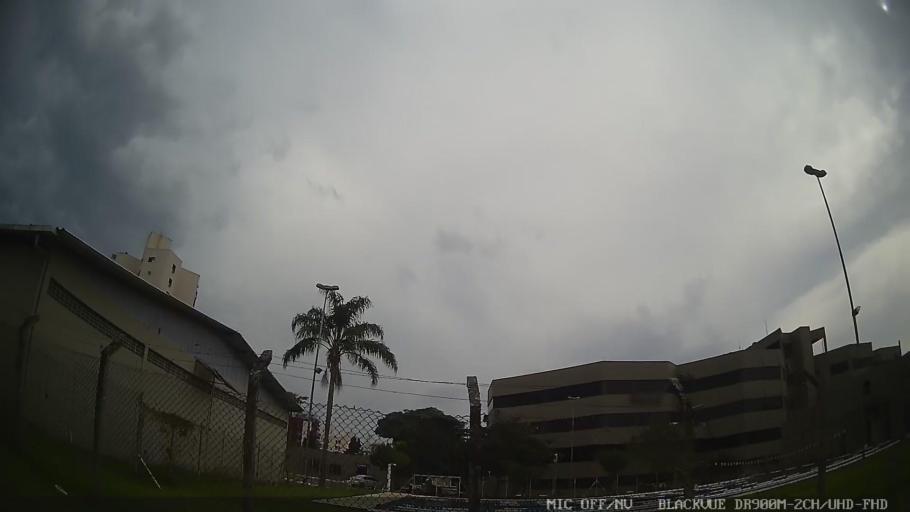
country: BR
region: Sao Paulo
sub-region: Guaruja
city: Guaruja
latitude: -23.9776
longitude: -46.2208
